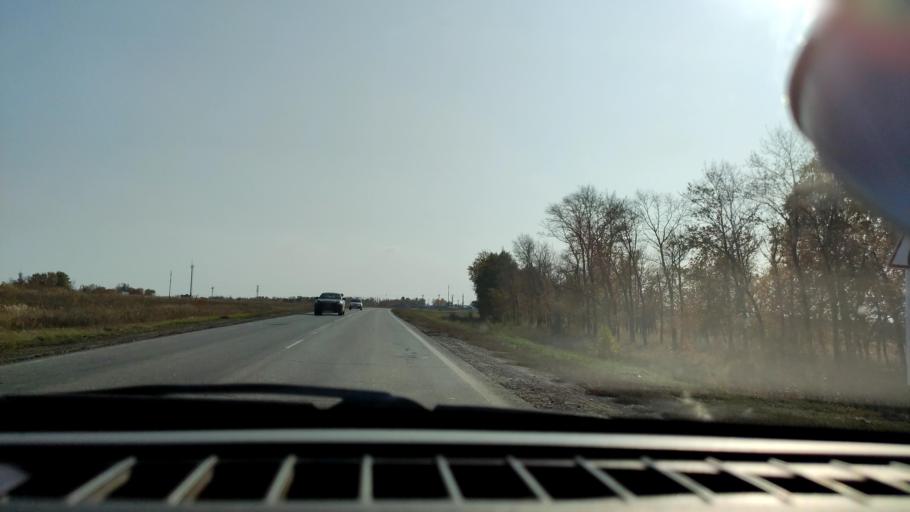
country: RU
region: Samara
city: Dubovyy Umet
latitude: 53.0891
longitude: 50.3493
